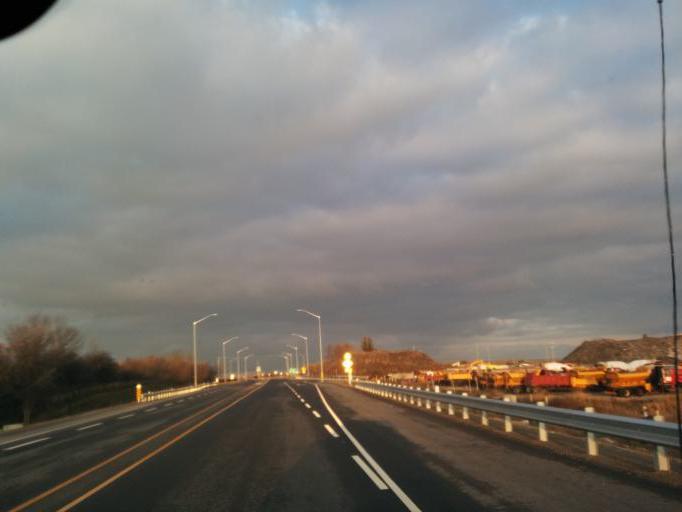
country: CA
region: Ontario
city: Brampton
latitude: 43.8960
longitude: -79.7683
